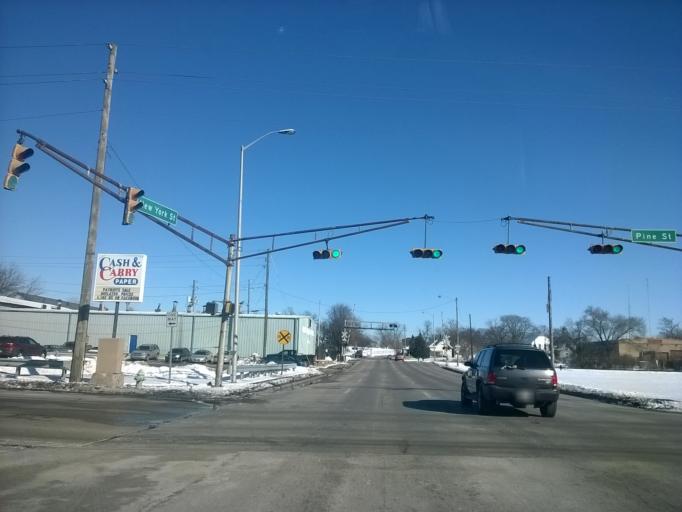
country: US
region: Indiana
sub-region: Marion County
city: Indianapolis
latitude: 39.7710
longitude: -86.1424
